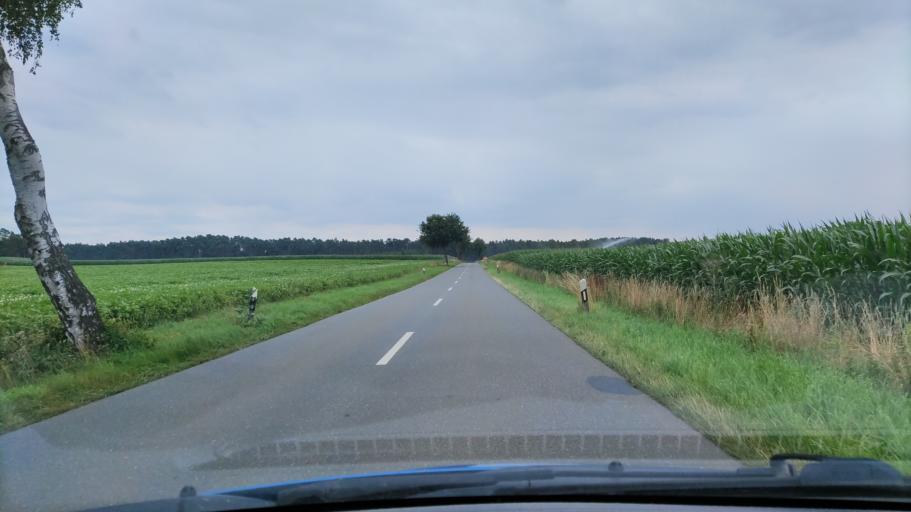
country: DE
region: Lower Saxony
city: Rosche
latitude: 53.0243
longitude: 10.7664
